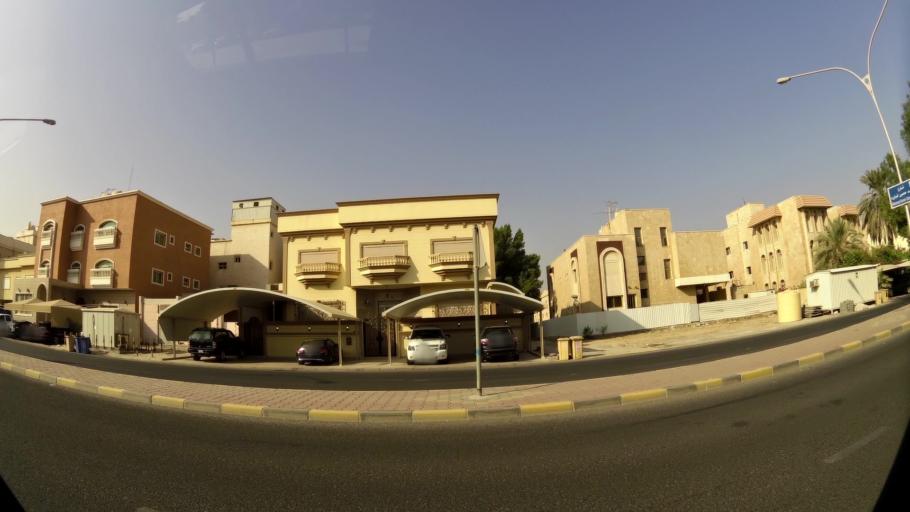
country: KW
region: Muhafazat Hawalli
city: Hawalli
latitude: 29.3226
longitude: 48.0385
